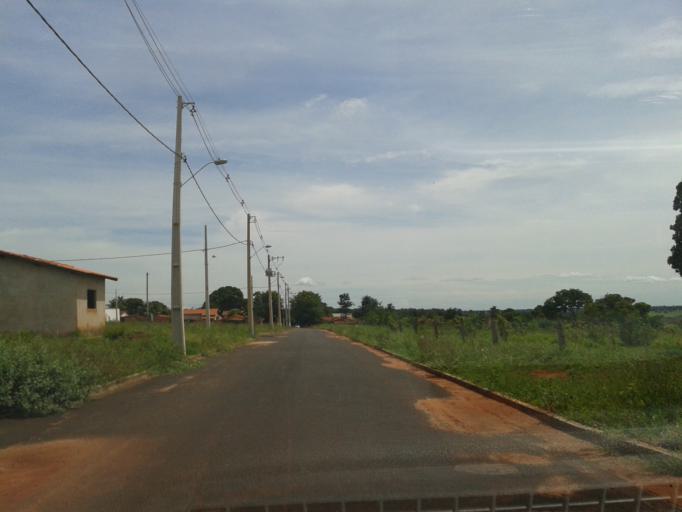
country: BR
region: Minas Gerais
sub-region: Santa Vitoria
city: Santa Vitoria
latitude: -18.8383
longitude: -50.1352
